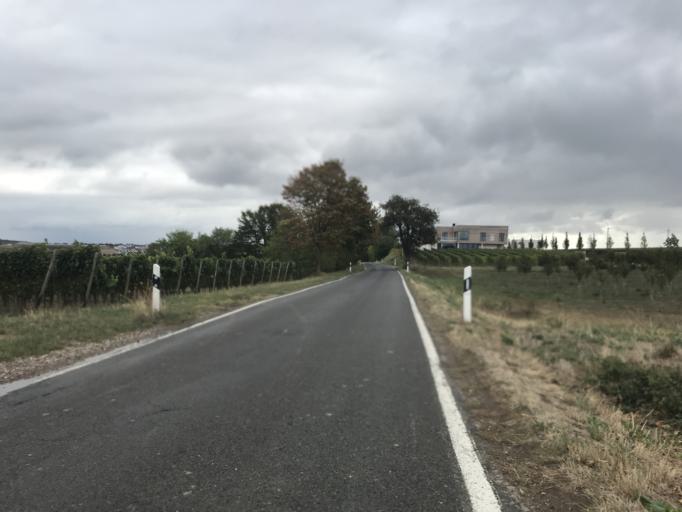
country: DE
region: Rheinland-Pfalz
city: Ober-Saulheim
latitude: 49.8839
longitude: 8.1377
